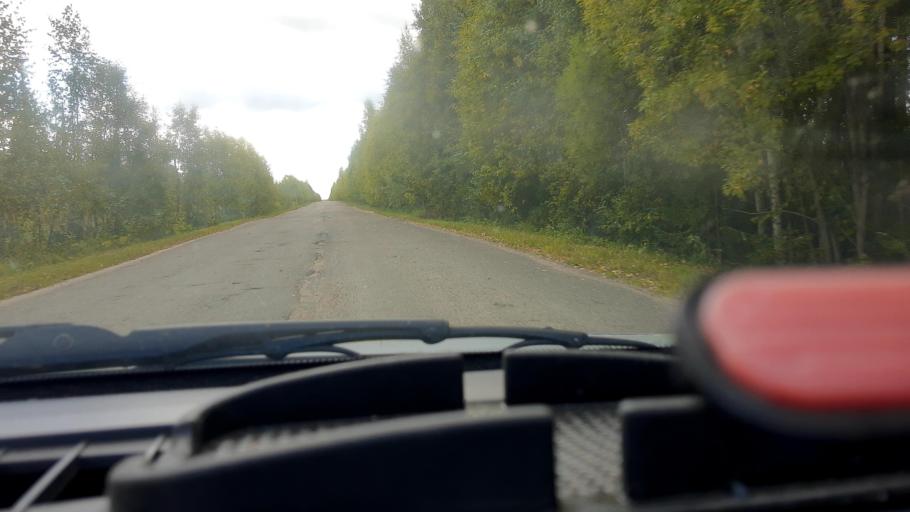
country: RU
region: Mariy-El
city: Kilemary
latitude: 56.9040
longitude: 46.7383
